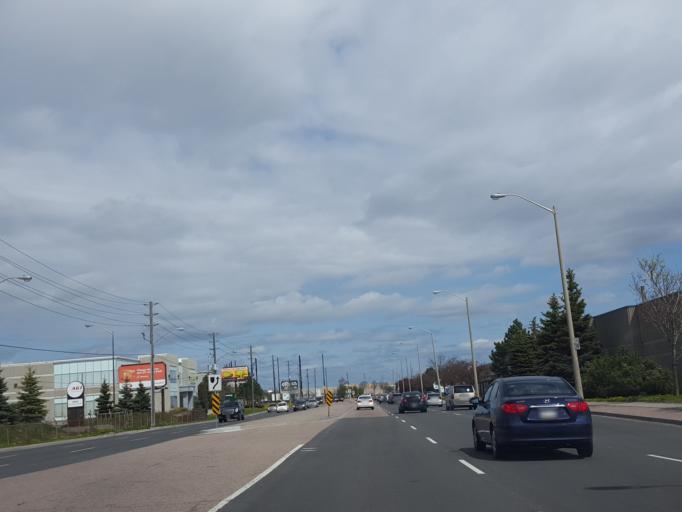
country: CA
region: Ontario
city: Markham
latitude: 43.8271
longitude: -79.2491
